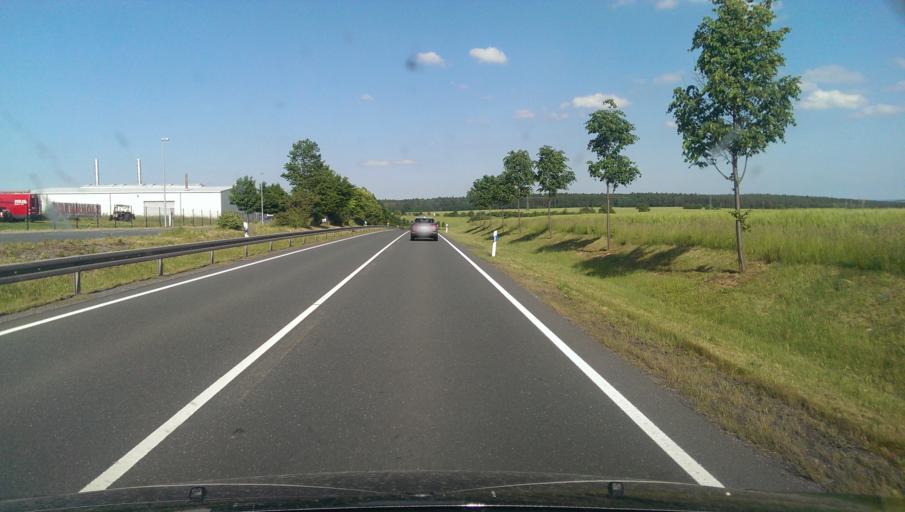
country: DE
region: Thuringia
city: Lederhose
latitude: 50.8051
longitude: 11.9143
